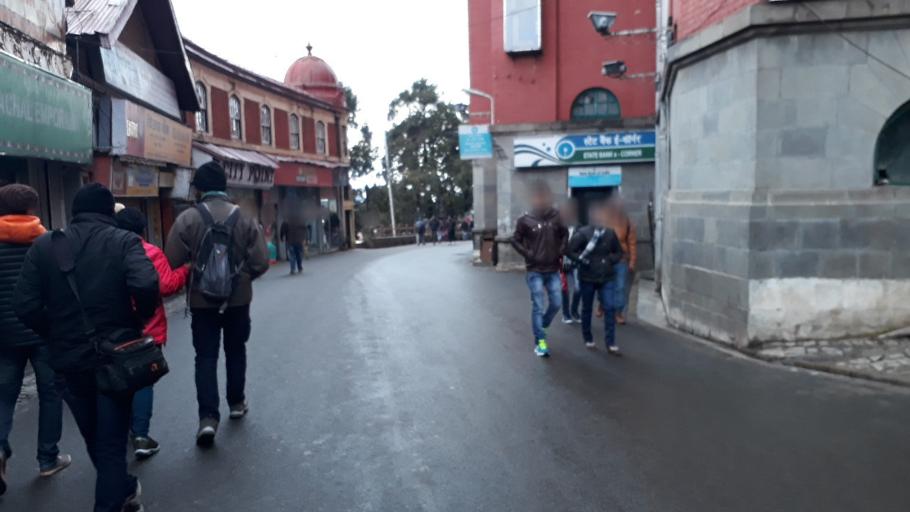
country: IN
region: Himachal Pradesh
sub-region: Shimla
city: Shimla
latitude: 31.1054
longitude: 77.1707
